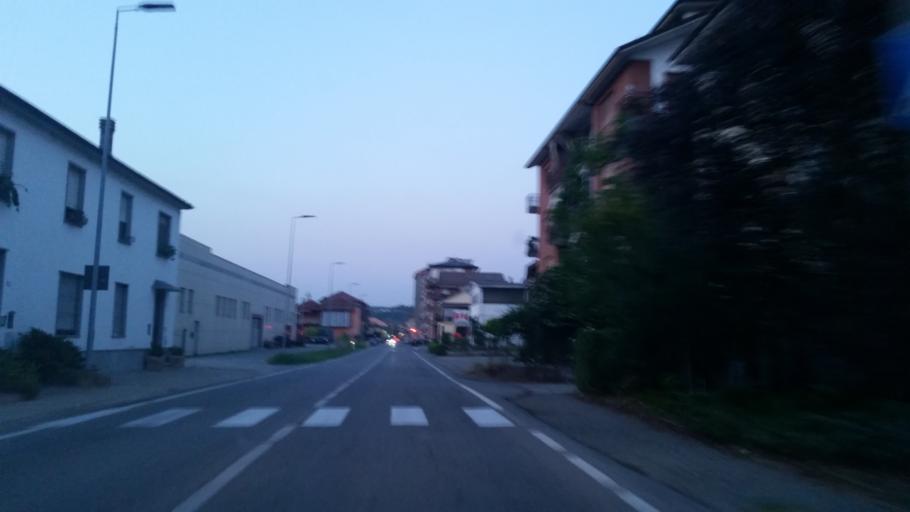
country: IT
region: Piedmont
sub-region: Provincia di Cuneo
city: Santo Stefano Belbo
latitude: 44.7047
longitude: 8.2248
